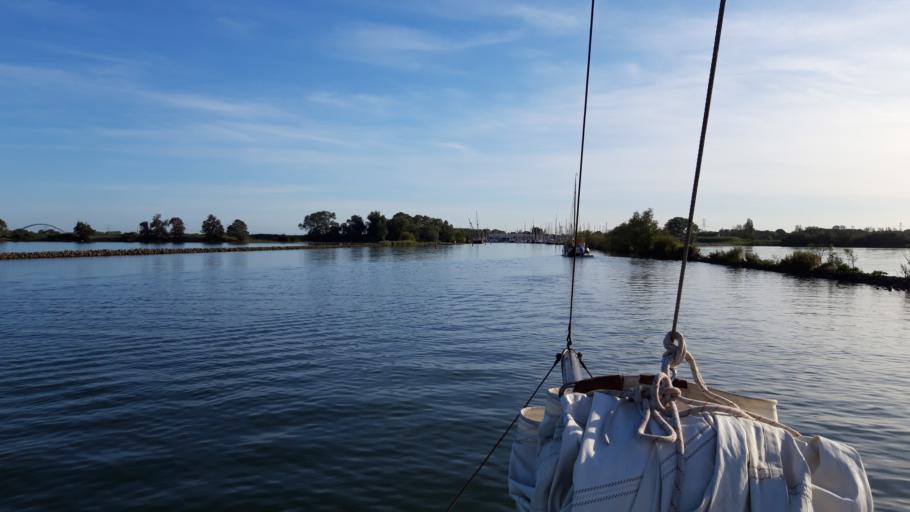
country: NL
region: North Holland
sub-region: Gemeente Weesp
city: Weesp
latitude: 52.3415
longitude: 5.0689
